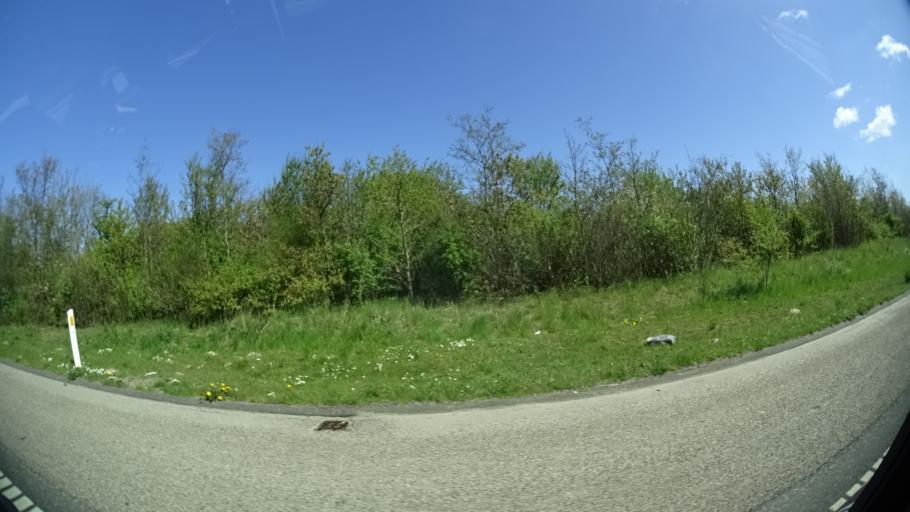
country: DK
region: Central Jutland
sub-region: Skanderborg Kommune
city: Horning
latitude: 56.1137
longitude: 10.0392
